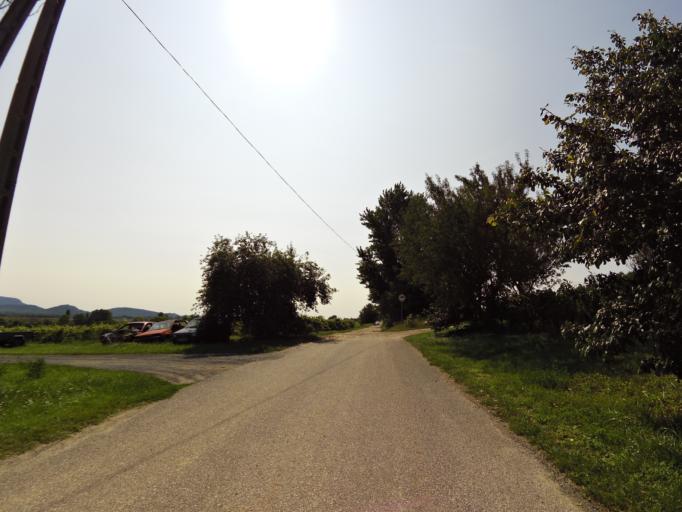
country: HU
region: Veszprem
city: Tapolca
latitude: 46.8227
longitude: 17.3733
